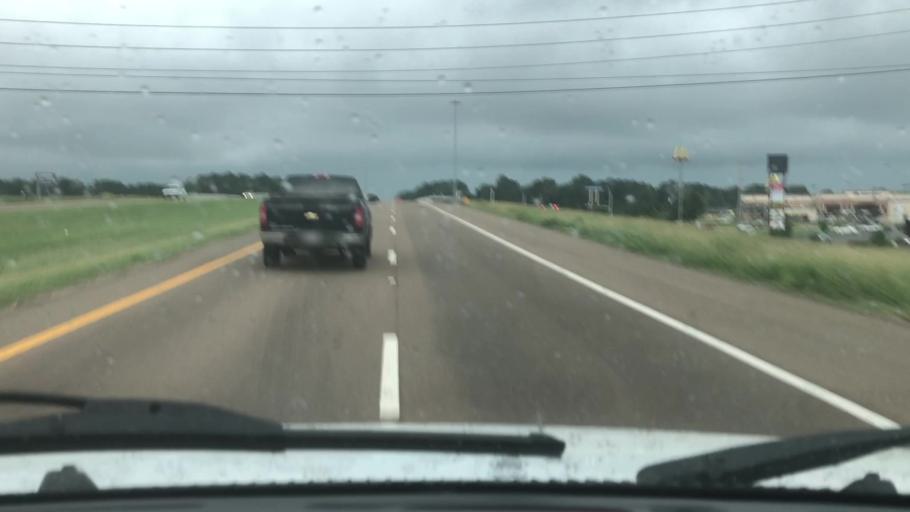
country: US
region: Texas
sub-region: Bowie County
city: Wake Village
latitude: 33.4205
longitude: -94.0967
